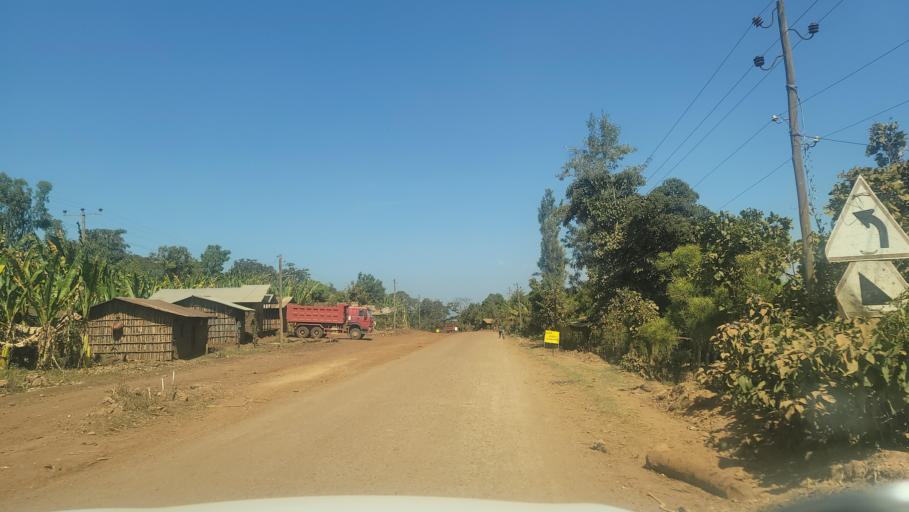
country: ET
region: Oromiya
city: Agaro
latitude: 7.8252
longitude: 36.5403
